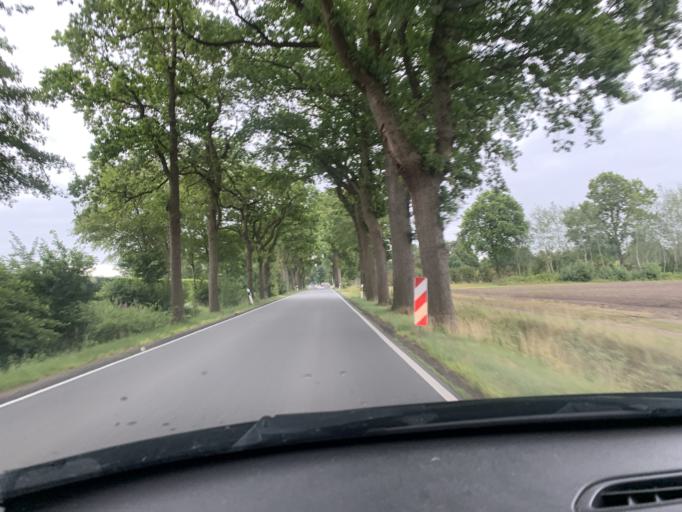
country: DE
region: Lower Saxony
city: Westerstede
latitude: 53.2550
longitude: 7.9597
